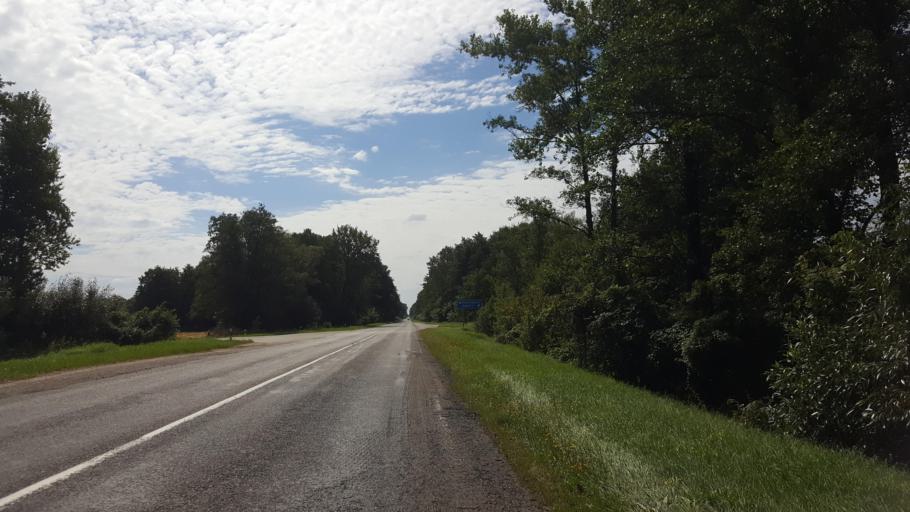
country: BY
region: Brest
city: Zhabinka
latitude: 52.2869
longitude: 23.9438
